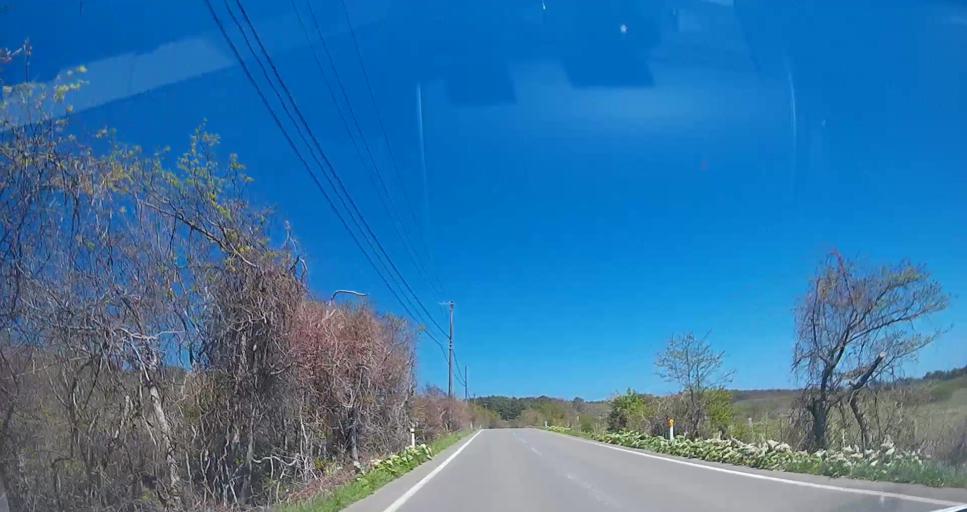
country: JP
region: Aomori
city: Mutsu
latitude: 41.2564
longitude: 141.3886
